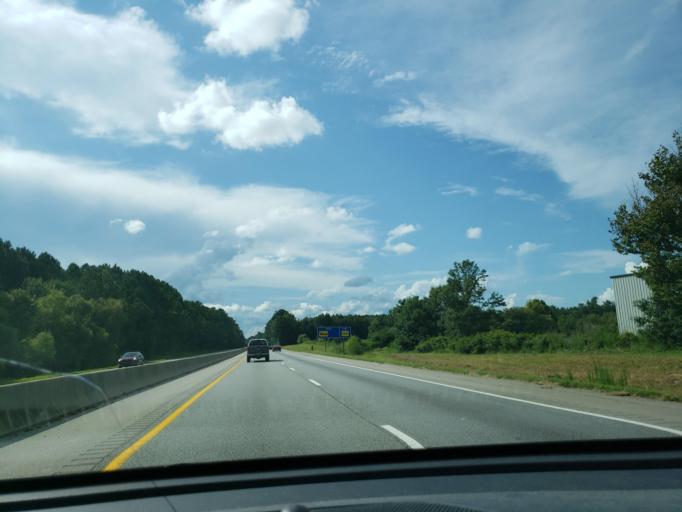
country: US
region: Virginia
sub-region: City of Franklin
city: Franklin
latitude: 36.6547
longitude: -76.9258
